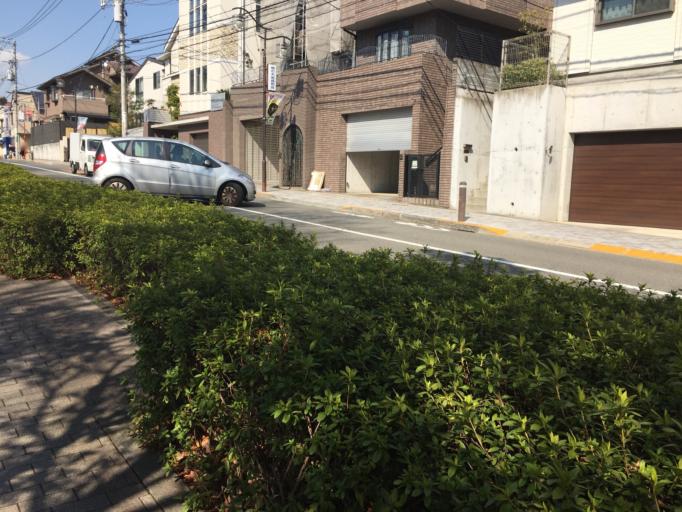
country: JP
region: Tokyo
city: Tokyo
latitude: 35.6206
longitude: 139.6742
